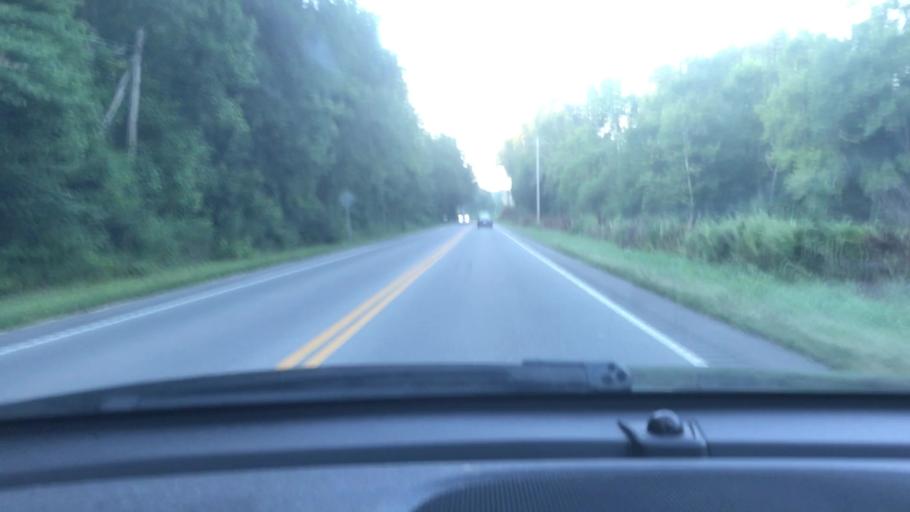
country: US
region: Tennessee
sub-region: Dickson County
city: Dickson
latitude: 36.1152
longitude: -87.3678
